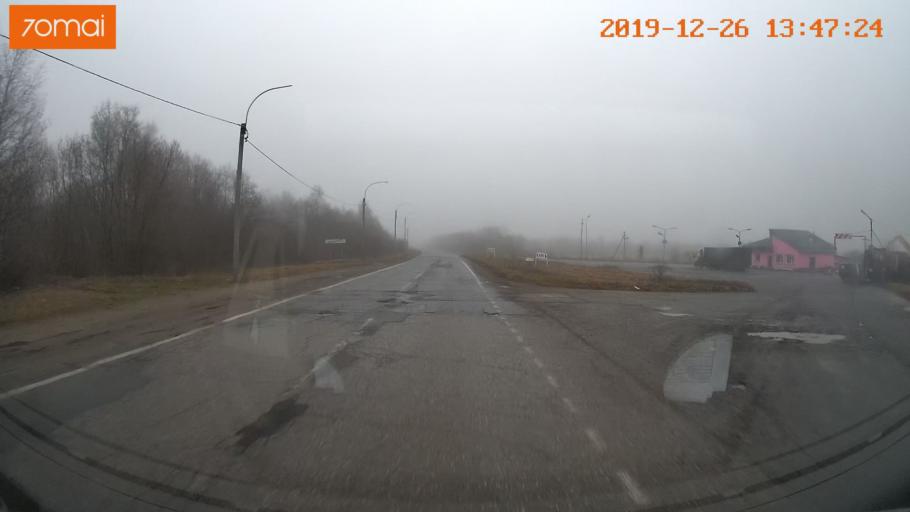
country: RU
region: Vologda
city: Sheksna
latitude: 58.6851
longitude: 38.5338
